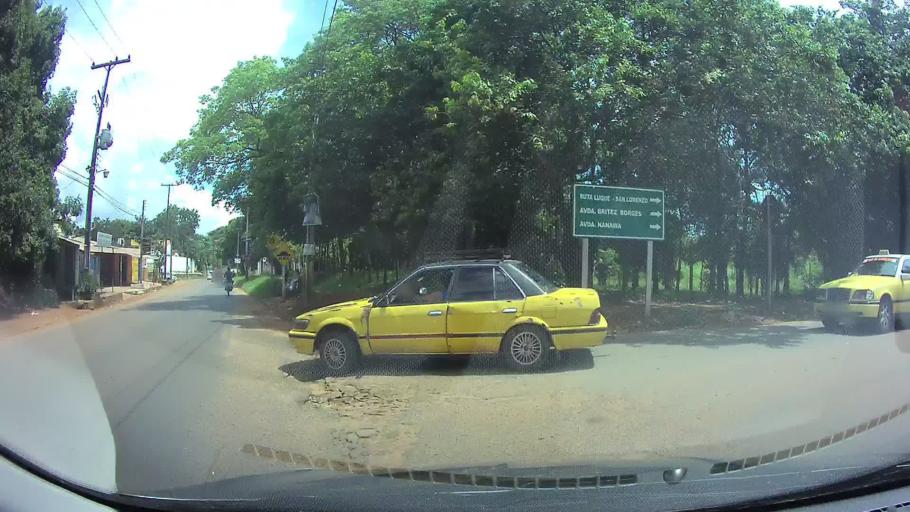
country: PY
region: Central
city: San Lorenzo
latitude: -25.3050
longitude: -57.4913
